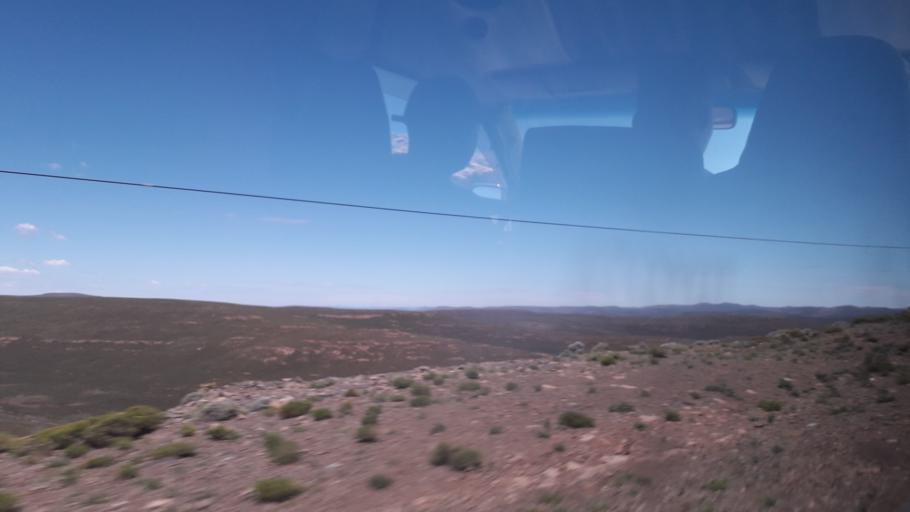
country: LS
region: Mokhotlong
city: Mokhotlong
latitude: -29.0248
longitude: 28.8581
